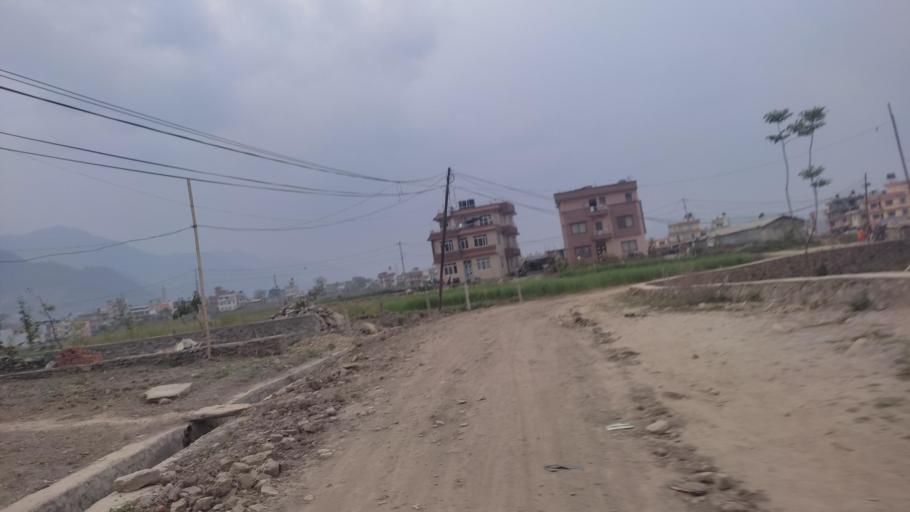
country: NP
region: Central Region
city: Kirtipur
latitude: 27.6634
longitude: 85.2772
